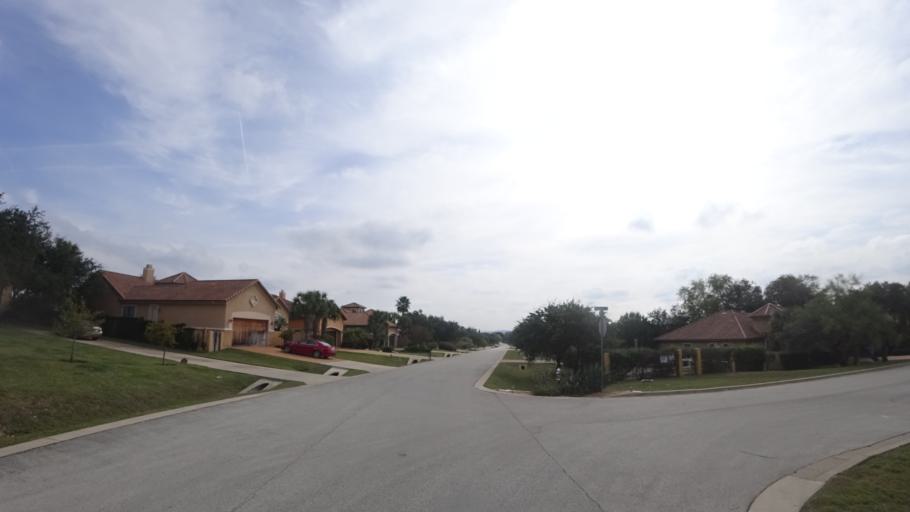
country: US
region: Texas
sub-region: Travis County
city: Hudson Bend
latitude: 30.3891
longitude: -97.9317
